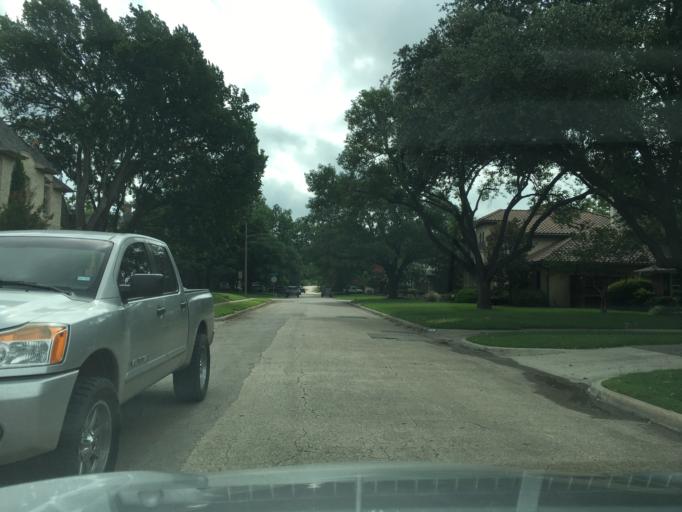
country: US
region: Texas
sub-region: Dallas County
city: University Park
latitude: 32.8832
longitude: -96.7914
